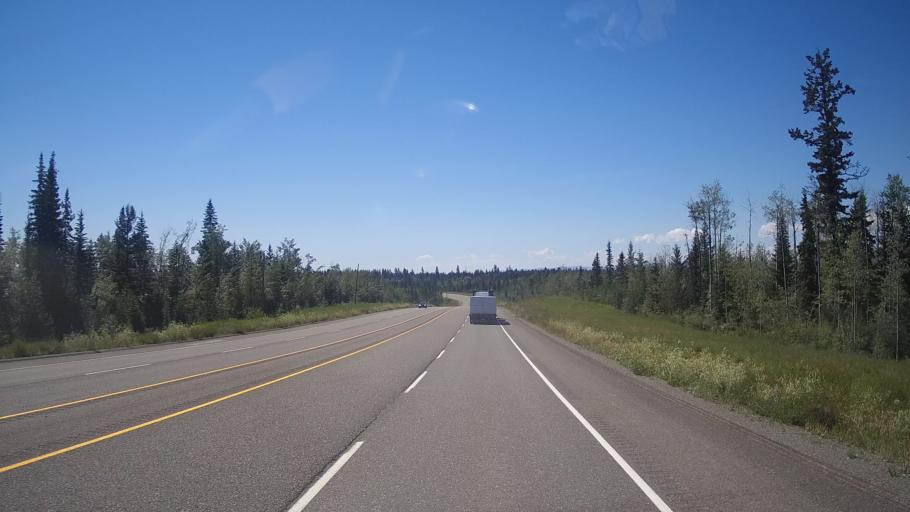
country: CA
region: British Columbia
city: Cache Creek
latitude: 51.4295
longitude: -121.3764
